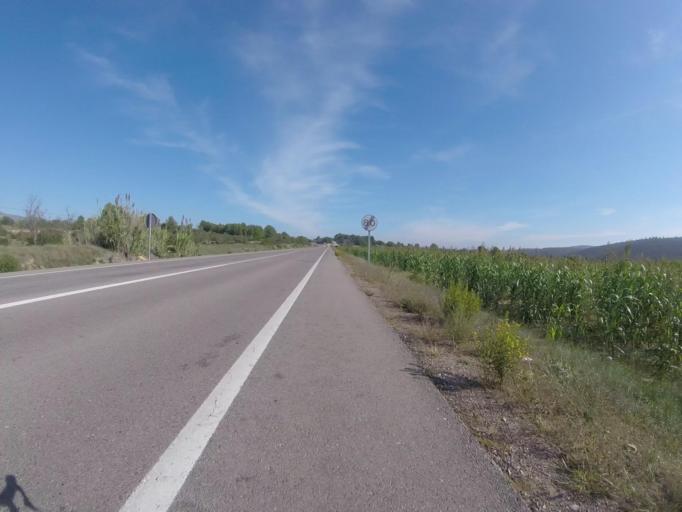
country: ES
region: Valencia
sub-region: Provincia de Castello
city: Benlloch
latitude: 40.2548
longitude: 0.0759
